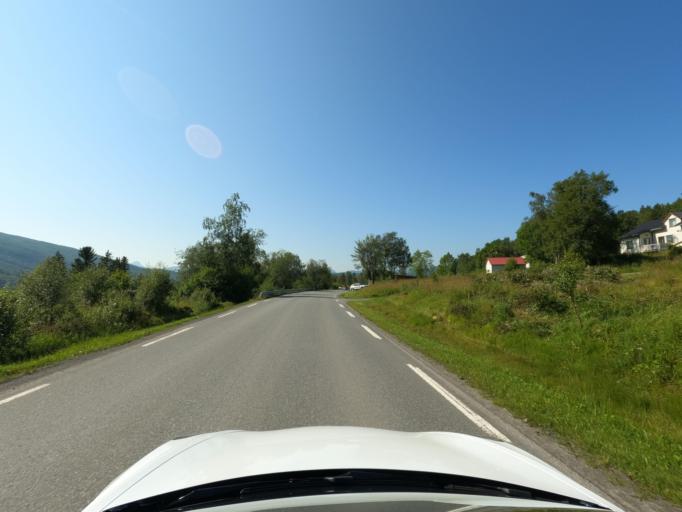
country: NO
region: Nordland
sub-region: Ballangen
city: Ballangen
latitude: 68.3463
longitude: 16.8445
